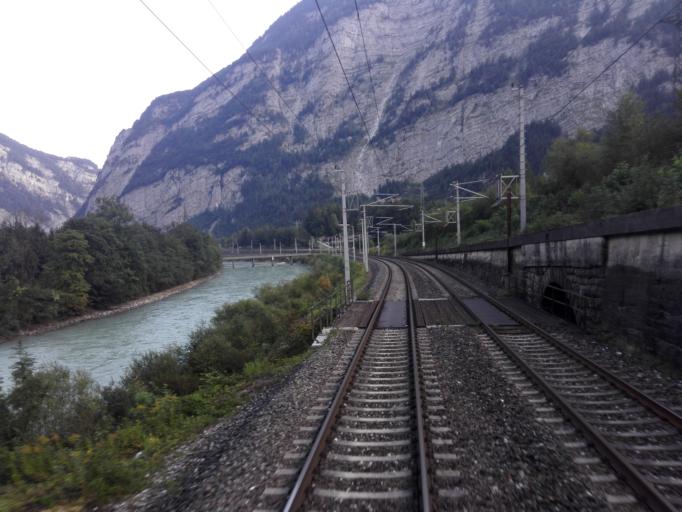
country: AT
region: Salzburg
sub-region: Politischer Bezirk Hallein
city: Golling an der Salzach
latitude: 47.5386
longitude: 13.1697
